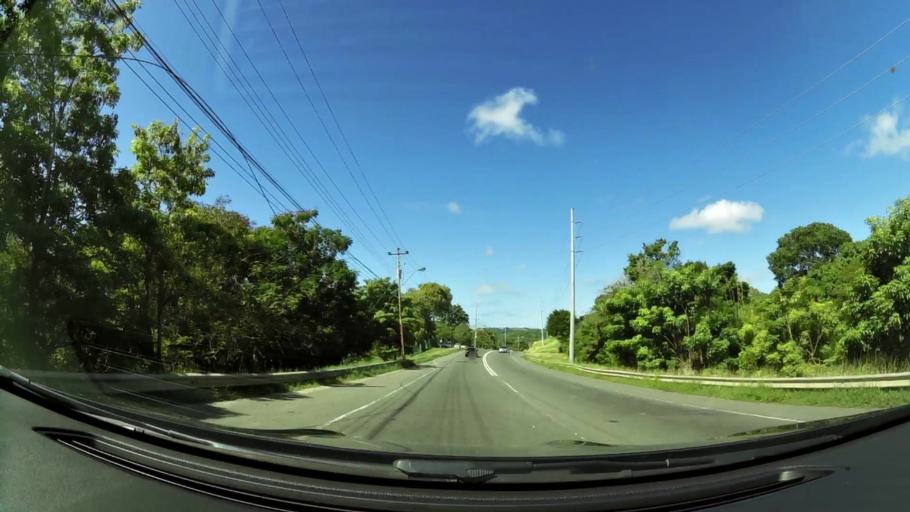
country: TT
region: Tobago
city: Scarborough
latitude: 11.1859
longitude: -60.7346
